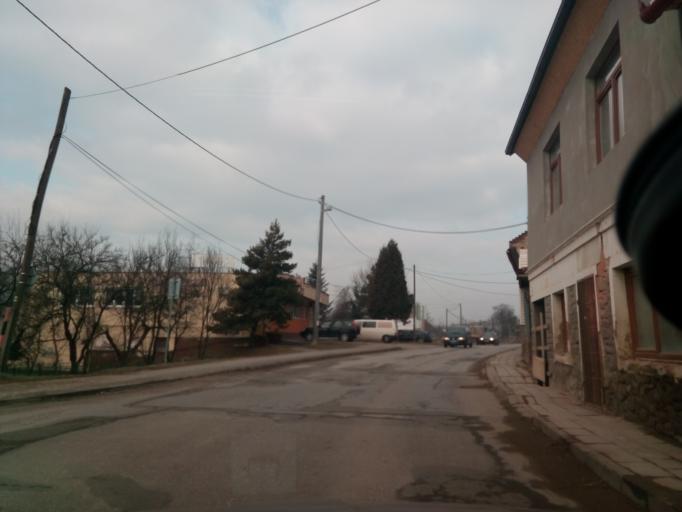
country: SK
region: Presovsky
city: Lipany
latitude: 49.1527
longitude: 20.9608
